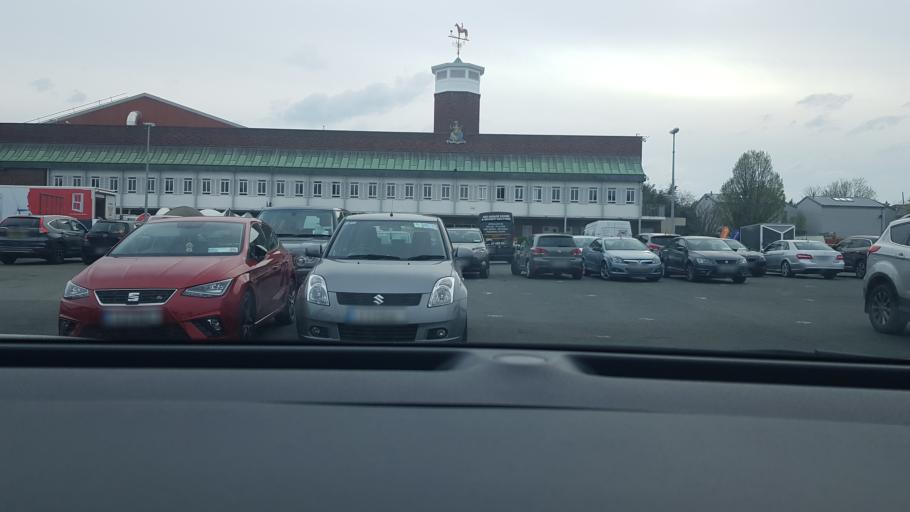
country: IE
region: Leinster
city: Donnybrook
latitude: 53.3238
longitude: -6.2246
